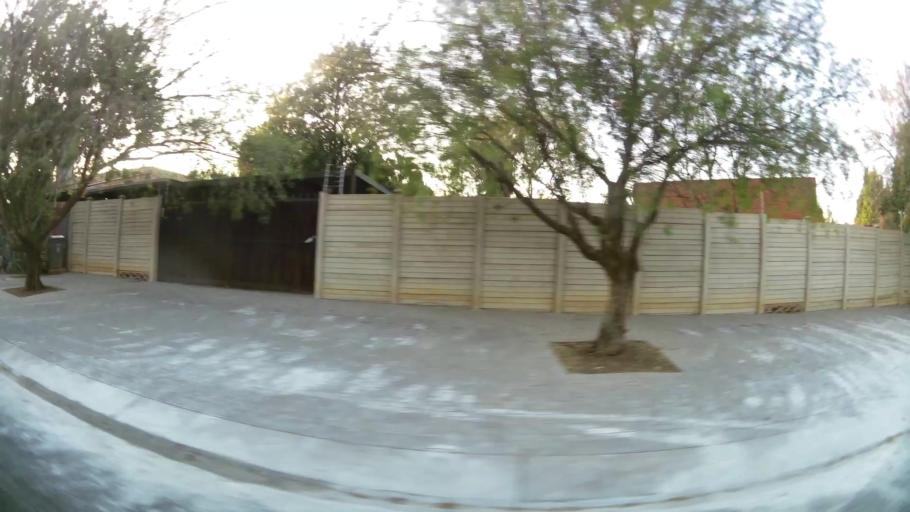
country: ZA
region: Orange Free State
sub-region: Mangaung Metropolitan Municipality
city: Bloemfontein
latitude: -29.1011
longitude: 26.1500
